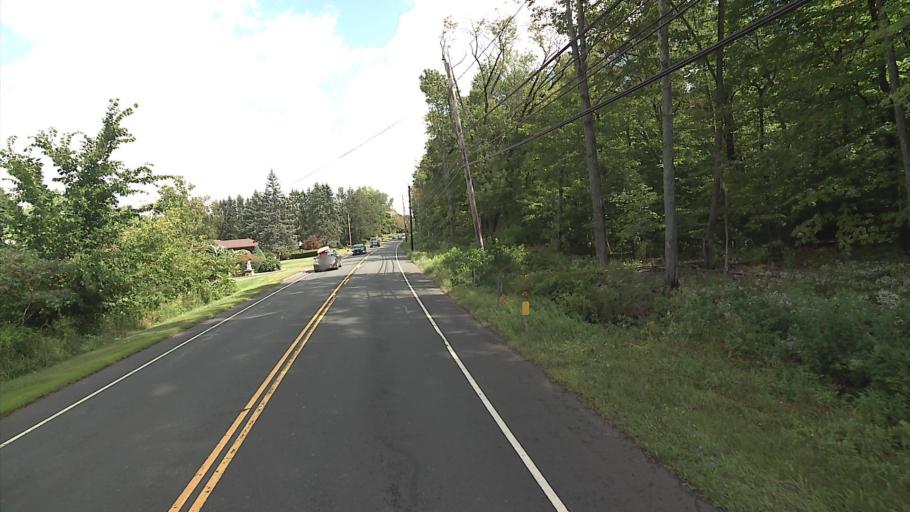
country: US
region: Connecticut
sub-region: Hartford County
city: Newington
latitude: 41.6516
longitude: -72.7074
